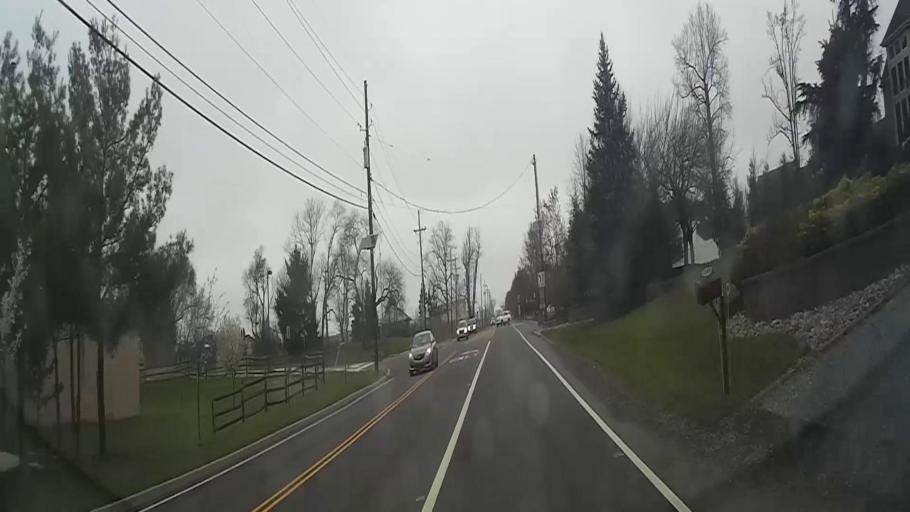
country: US
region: New Jersey
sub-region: Burlington County
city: Marlton
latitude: 39.8697
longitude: -74.8950
